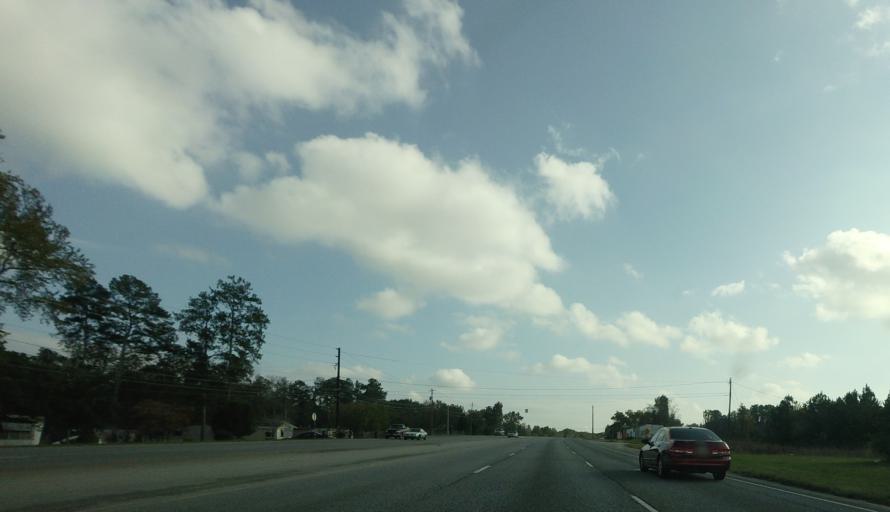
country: US
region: Georgia
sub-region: Bibb County
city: Macon
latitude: 32.7510
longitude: -83.6580
